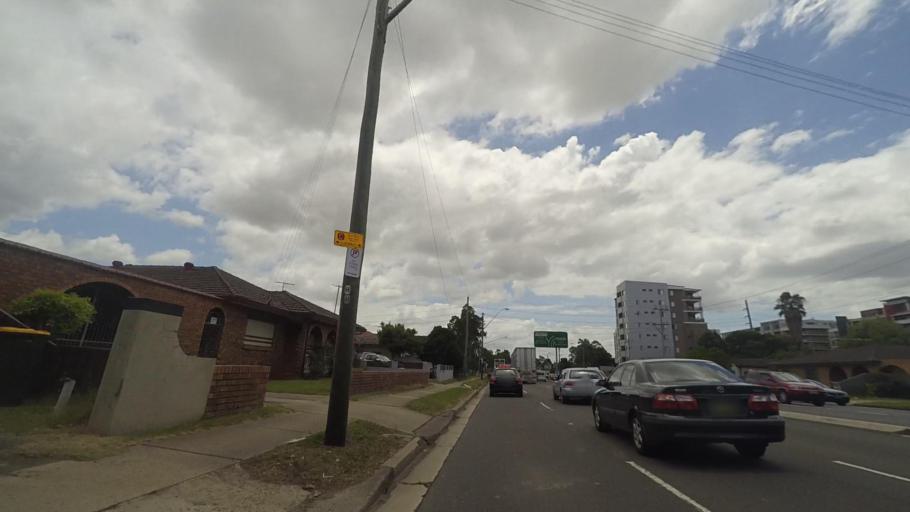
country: AU
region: New South Wales
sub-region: Fairfield
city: Liverpool
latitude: -33.9181
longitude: 150.9196
